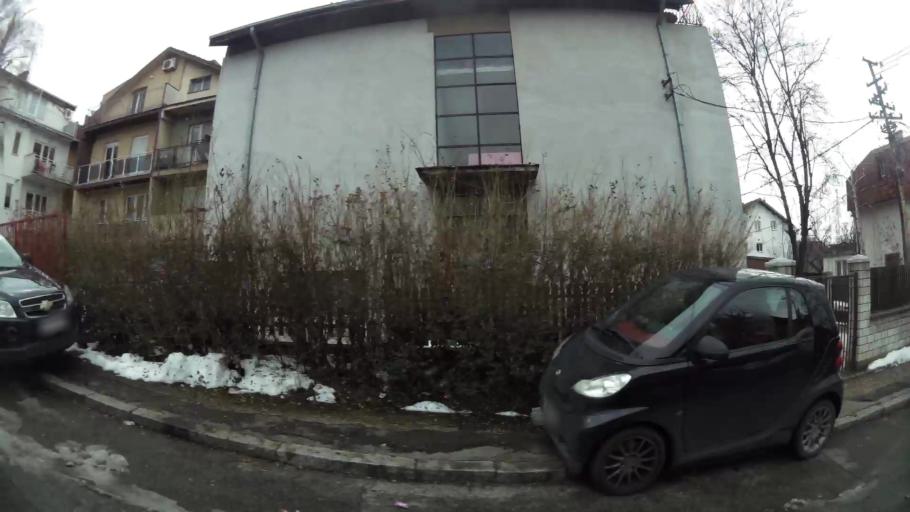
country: RS
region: Central Serbia
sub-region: Belgrade
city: Rakovica
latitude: 44.7512
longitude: 20.4107
